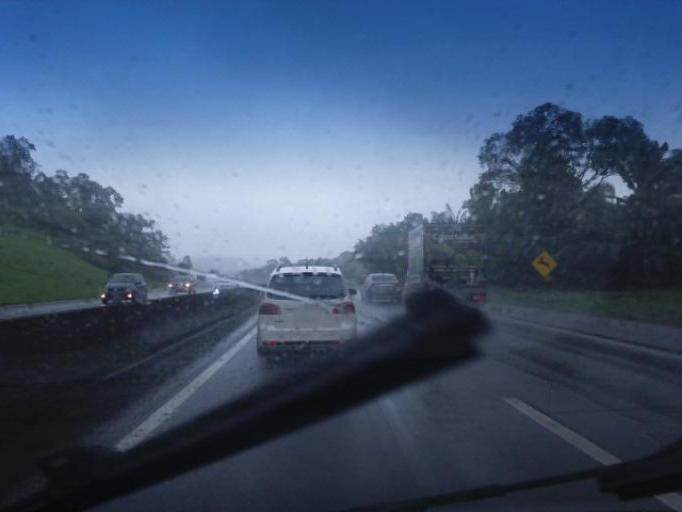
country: BR
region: Santa Catarina
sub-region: Joinville
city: Joinville
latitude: -26.1742
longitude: -48.9074
